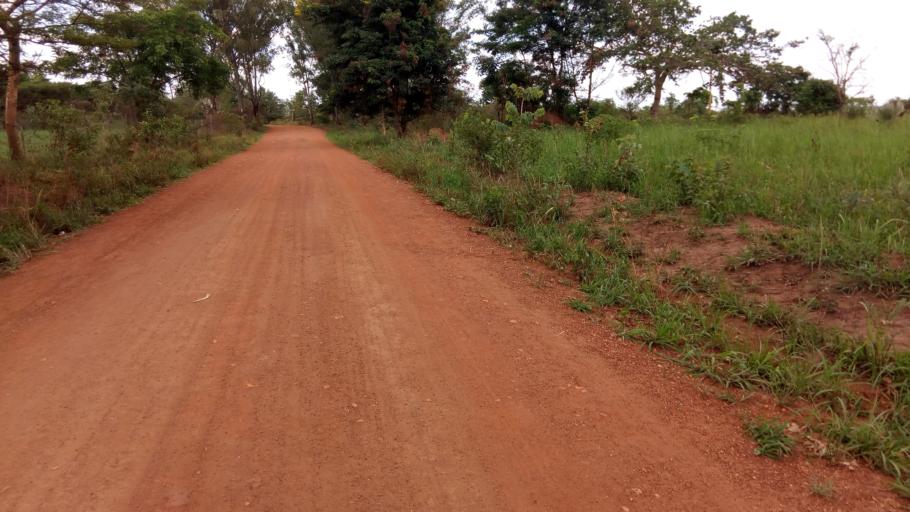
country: UG
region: Northern Region
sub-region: Gulu District
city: Gulu
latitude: 2.7874
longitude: 32.3487
